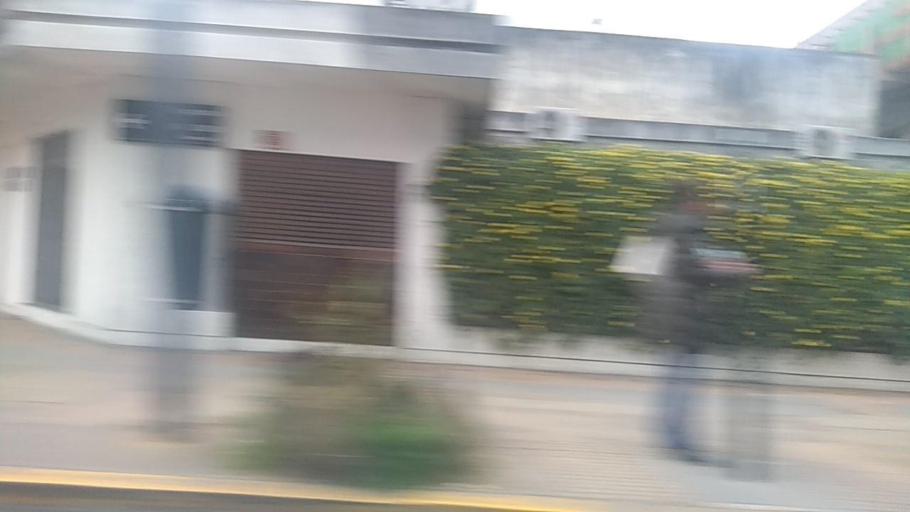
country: AR
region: Buenos Aires F.D.
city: Villa Santa Rita
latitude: -34.6021
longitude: -58.4984
